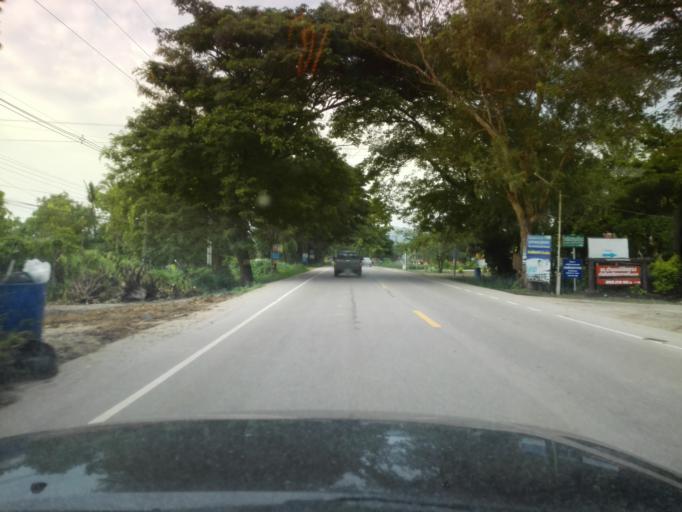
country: TH
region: Tak
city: Mae Sot
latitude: 16.8031
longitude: 98.5972
